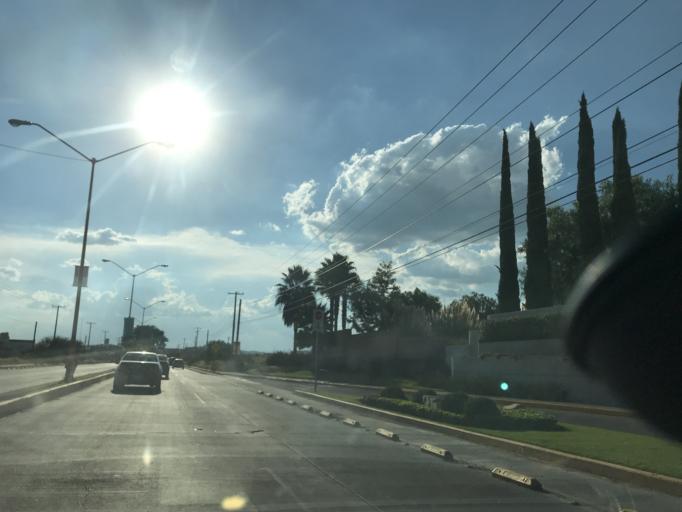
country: MX
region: Aguascalientes
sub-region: Aguascalientes
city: Pocitos
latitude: 21.9098
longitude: -102.3254
